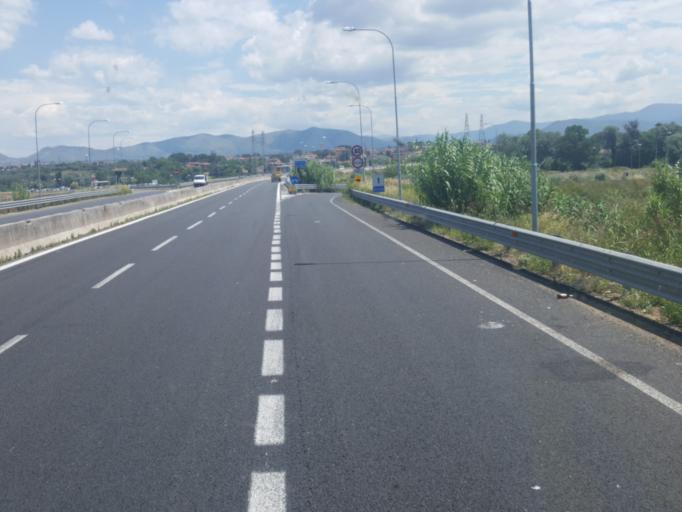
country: IT
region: Latium
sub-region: Citta metropolitana di Roma Capitale
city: Fiano Romano
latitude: 42.1525
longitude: 12.6397
